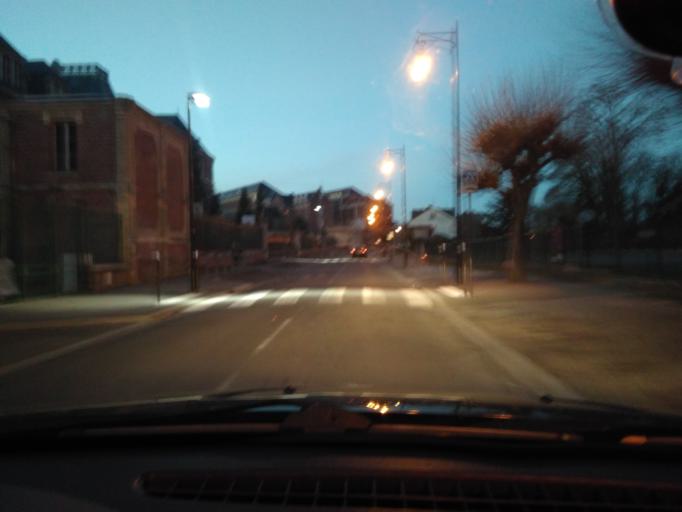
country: FR
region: Picardie
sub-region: Departement de l'Aisne
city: Laon
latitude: 49.5587
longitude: 3.6127
